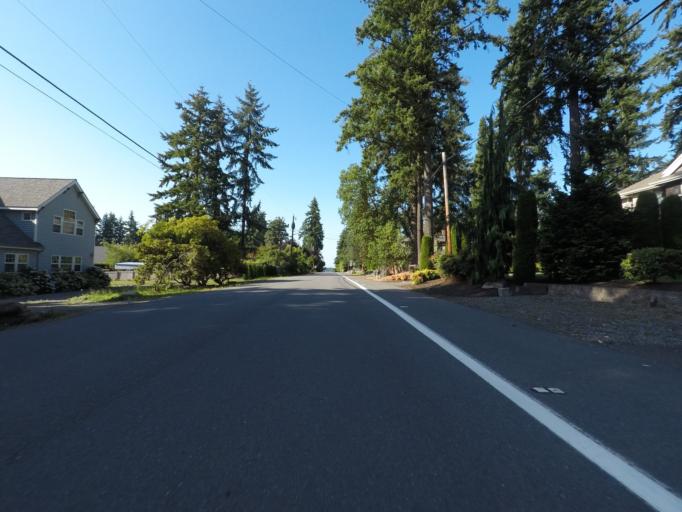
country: US
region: Washington
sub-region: King County
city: Inglewood-Finn Hill
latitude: 47.7384
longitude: -122.2328
